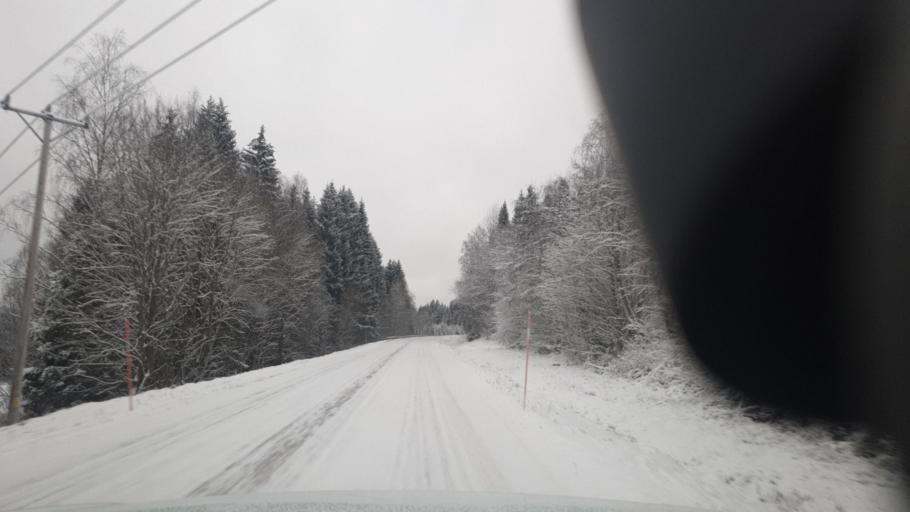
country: NO
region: Hedmark
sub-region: Eidskog
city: Skotterud
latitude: 59.7708
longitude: 12.0476
